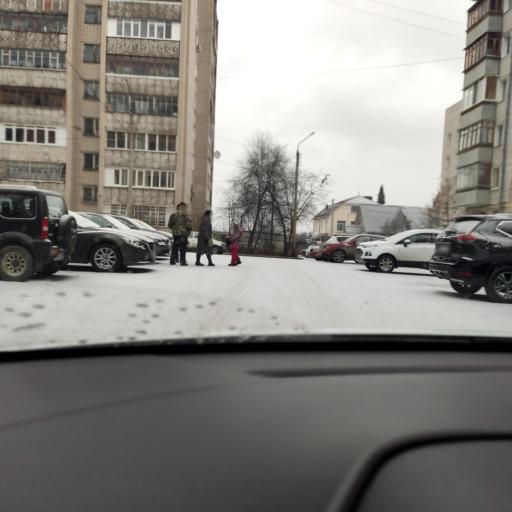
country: RU
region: Tatarstan
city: Vysokaya Gora
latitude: 55.8588
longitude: 49.2309
